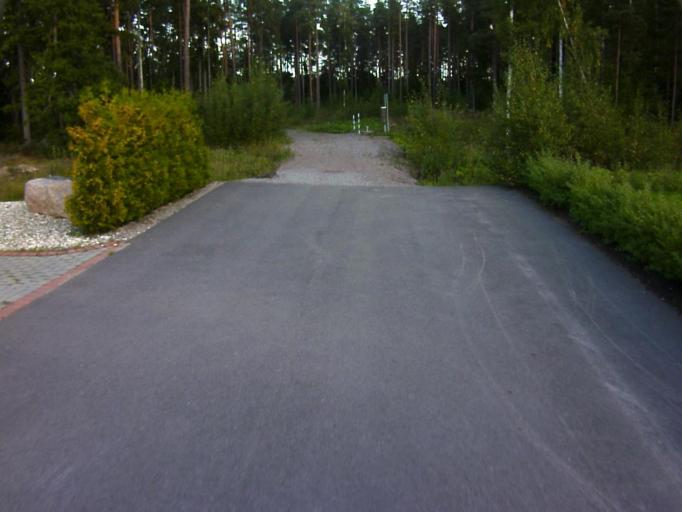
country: SE
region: Soedermanland
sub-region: Eskilstuna Kommun
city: Eskilstuna
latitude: 59.3862
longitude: 16.5478
